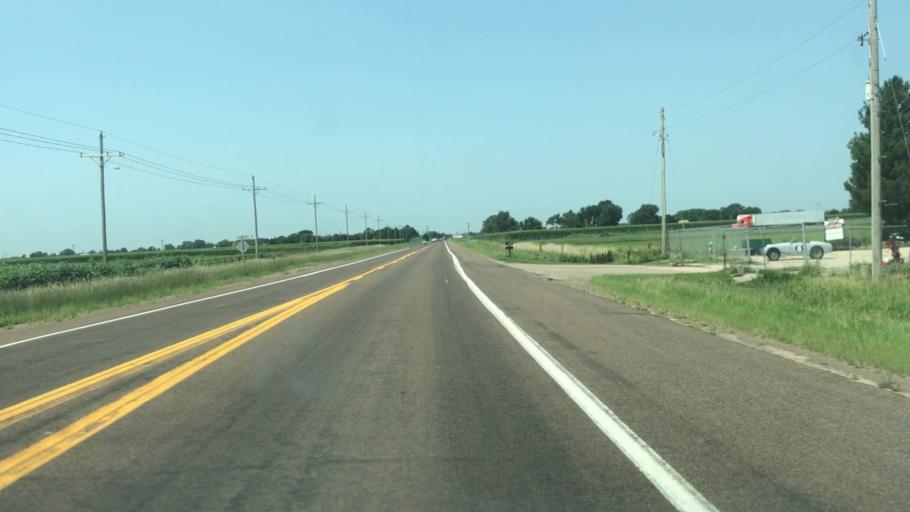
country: US
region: Nebraska
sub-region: Hall County
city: Grand Island
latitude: 40.8869
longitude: -98.3036
